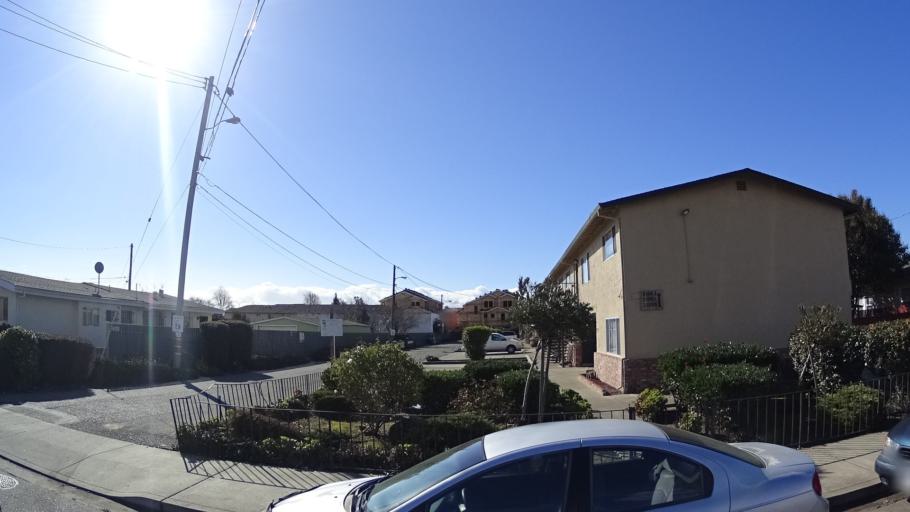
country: US
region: California
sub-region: Alameda County
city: Cherryland
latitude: 37.6671
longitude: -122.1139
